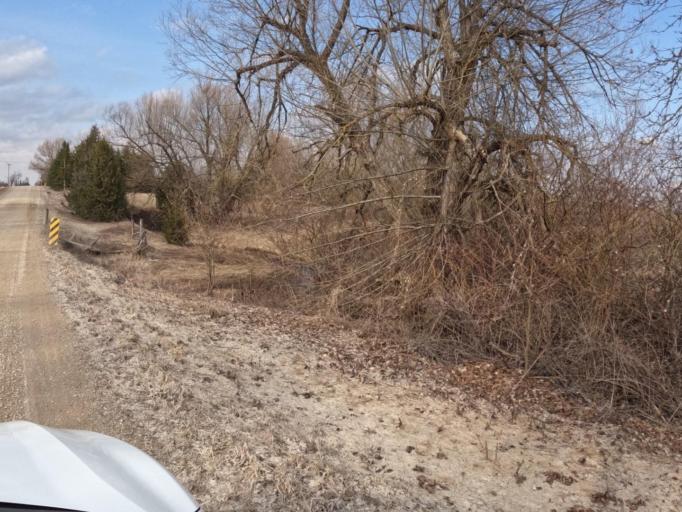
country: CA
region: Ontario
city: Shelburne
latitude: 43.9223
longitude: -80.3064
